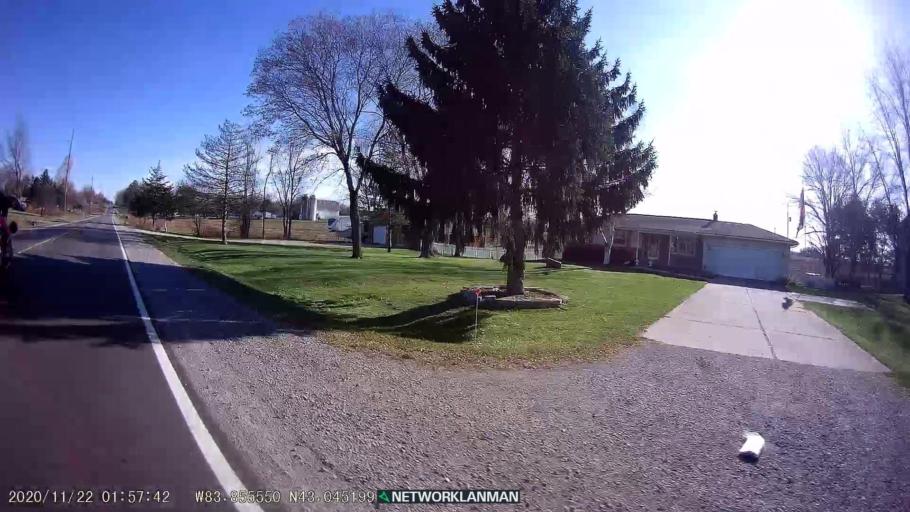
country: US
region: Michigan
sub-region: Genesee County
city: Flushing
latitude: 43.0449
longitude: -83.8552
